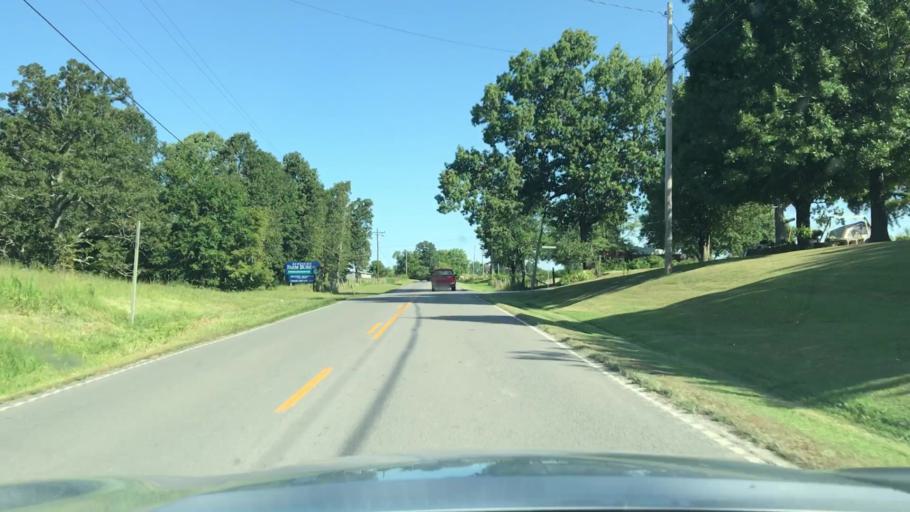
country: US
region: Kentucky
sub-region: Muhlenberg County
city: Greenville
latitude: 37.1699
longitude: -87.1499
